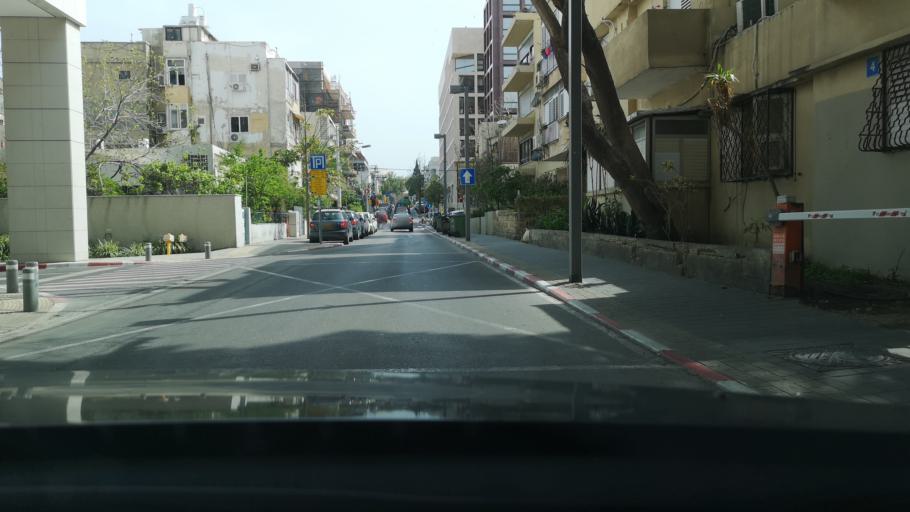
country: IL
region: Tel Aviv
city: Tel Aviv
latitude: 32.0649
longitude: 34.7676
